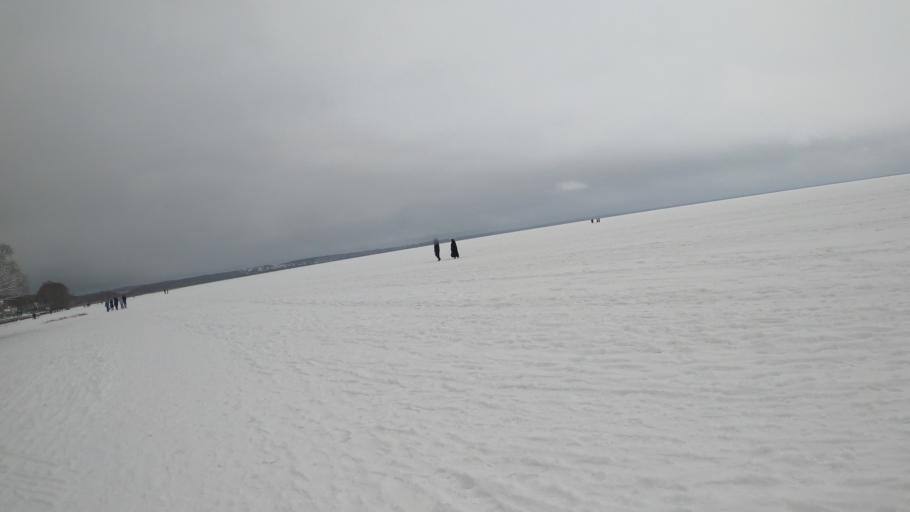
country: RU
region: Jaroslavl
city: Pereslavl'-Zalesskiy
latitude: 56.7370
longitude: 38.8286
